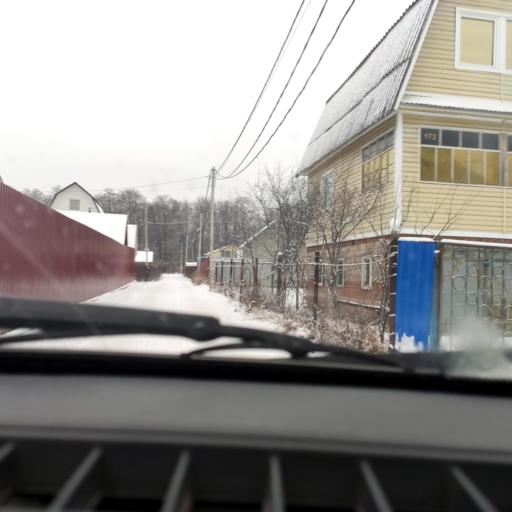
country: RU
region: Bashkortostan
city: Ufa
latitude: 54.6348
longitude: 55.8887
